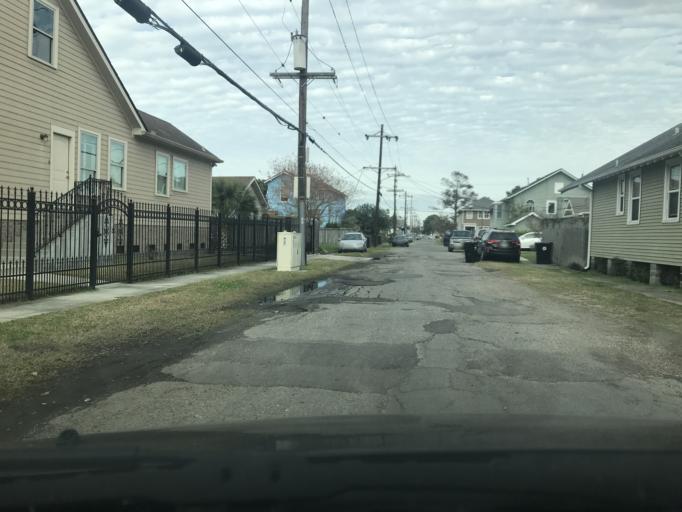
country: US
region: Louisiana
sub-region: Orleans Parish
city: New Orleans
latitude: 29.9507
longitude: -90.1055
